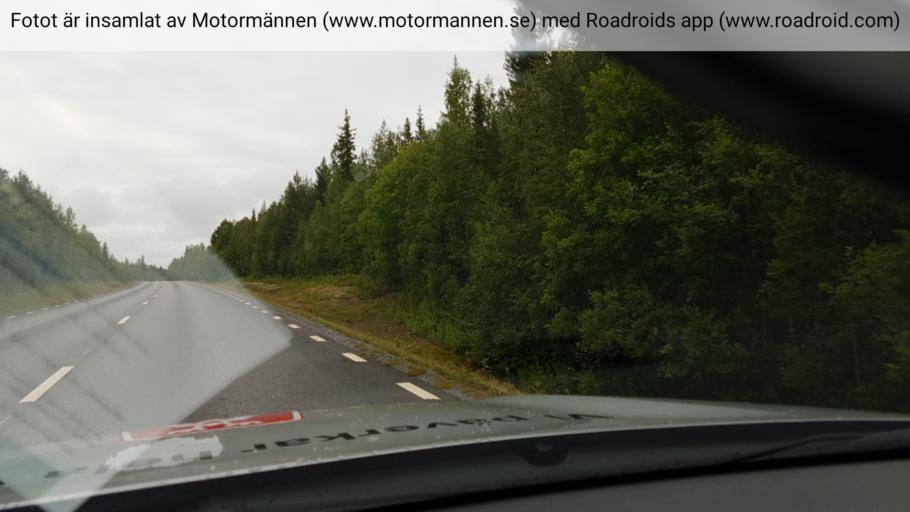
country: SE
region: Norrbotten
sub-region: Alvsbyns Kommun
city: AElvsbyn
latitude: 66.3172
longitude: 20.7886
